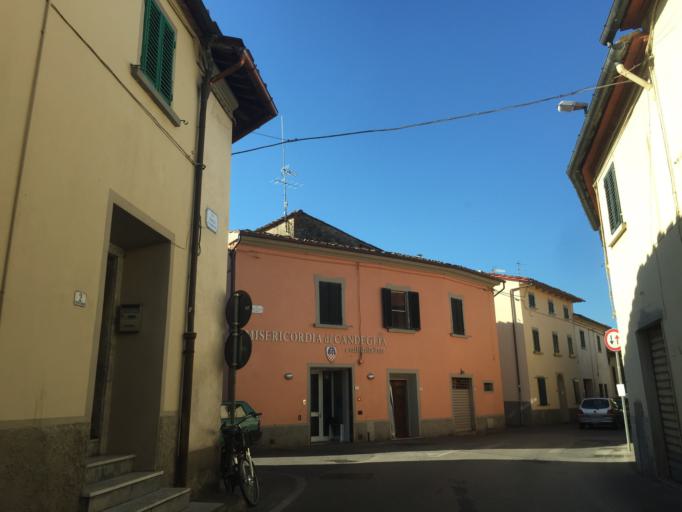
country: IT
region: Tuscany
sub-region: Provincia di Pistoia
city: Pistoia
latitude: 43.9544
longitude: 10.9422
